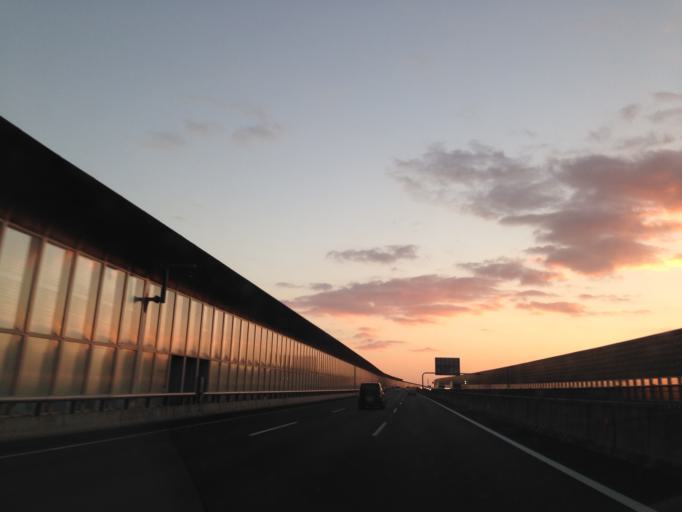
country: JP
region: Aichi
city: Obu
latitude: 35.0437
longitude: 136.9675
